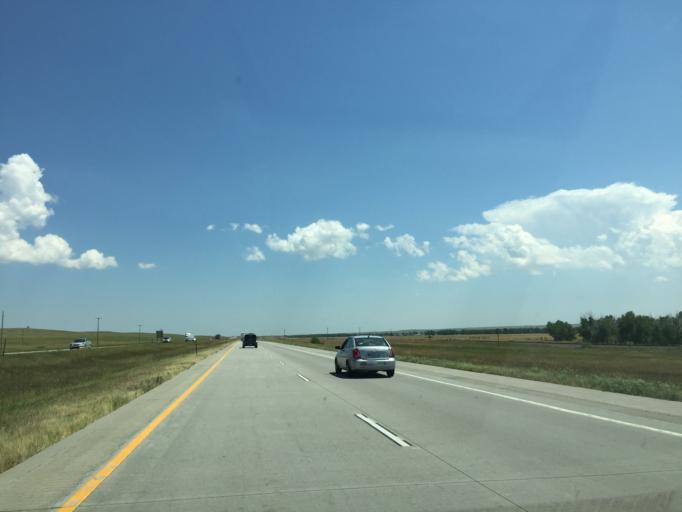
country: US
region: Colorado
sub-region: Lincoln County
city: Limon
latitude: 39.3012
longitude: -103.8129
